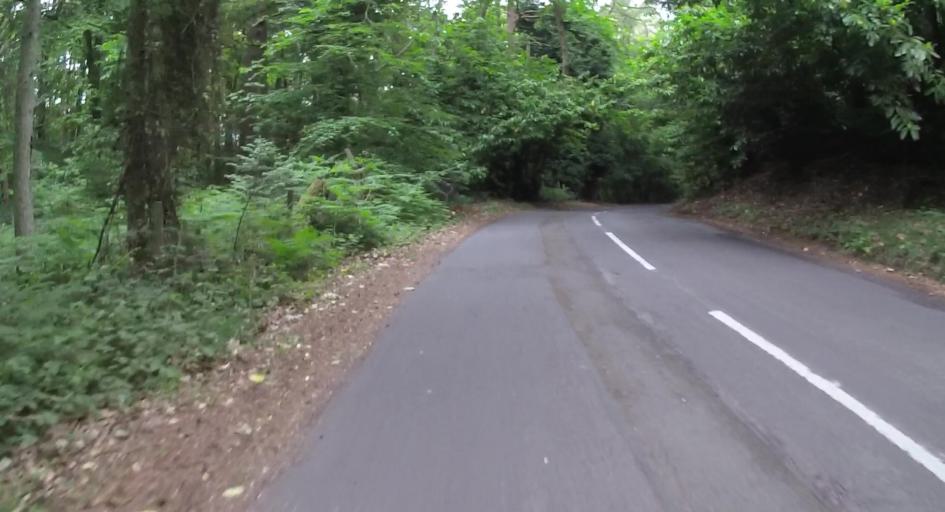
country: GB
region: England
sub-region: Surrey
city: Seale
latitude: 51.2093
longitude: -0.7466
